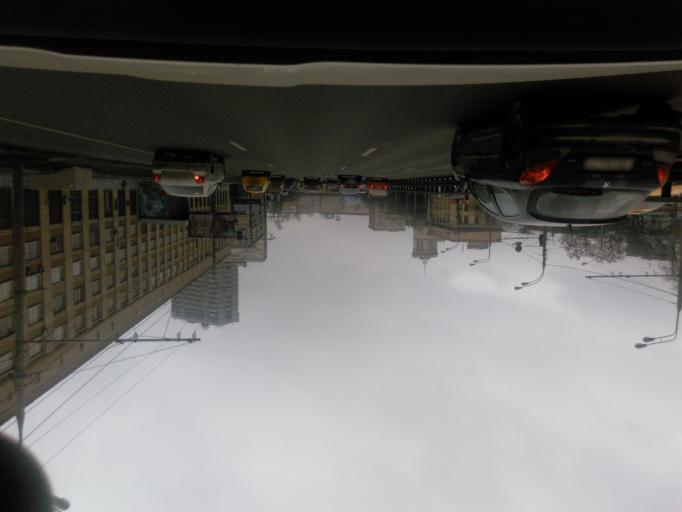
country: RU
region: Moskovskaya
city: Koptevo
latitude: 55.8115
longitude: 37.5038
